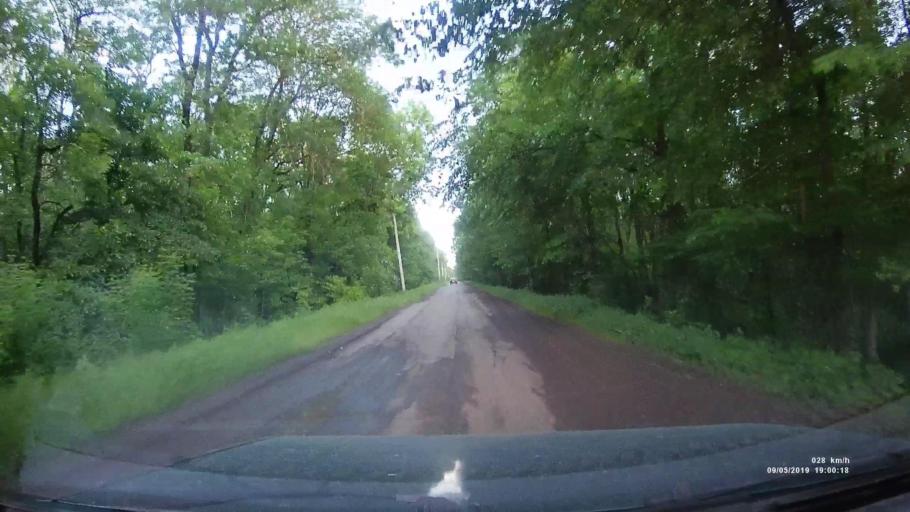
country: RU
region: Krasnodarskiy
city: Kanelovskaya
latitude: 46.7523
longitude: 39.1352
